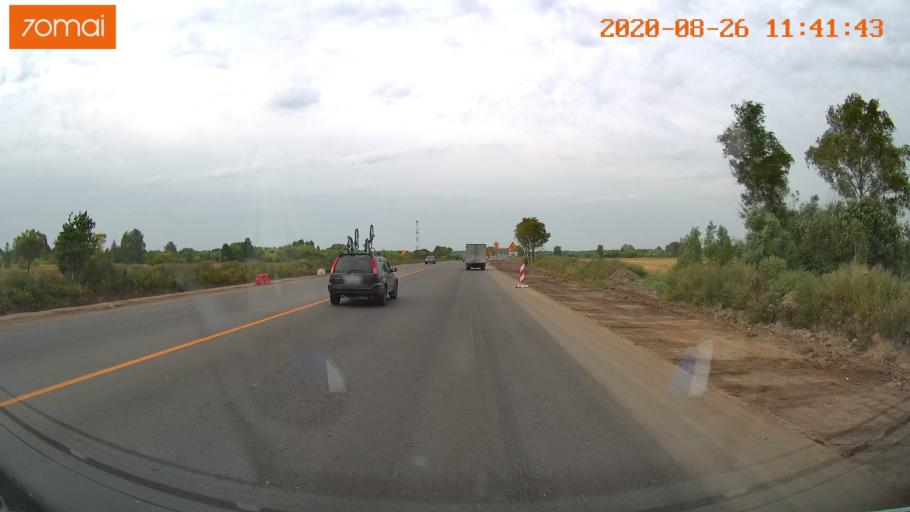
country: RU
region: Rjazan
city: Shilovo
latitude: 54.2957
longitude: 40.7060
